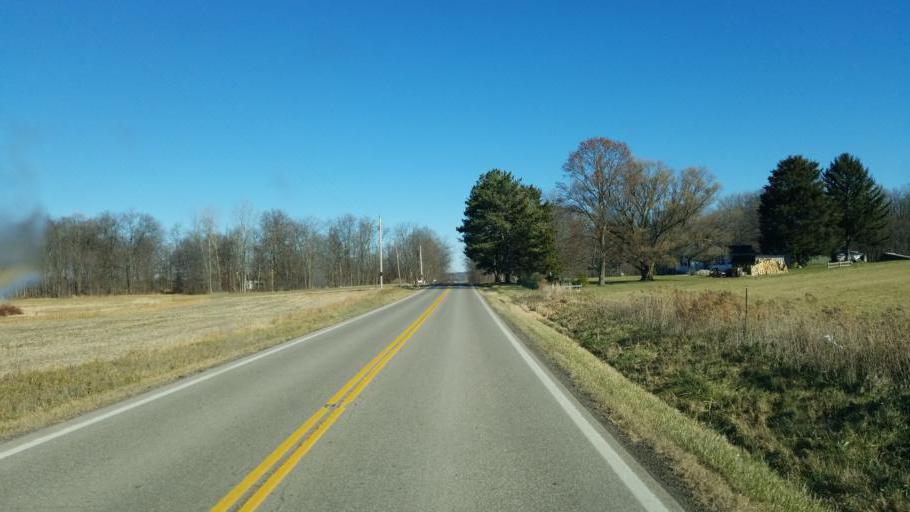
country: US
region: Ohio
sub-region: Ashland County
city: Ashland
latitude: 40.9432
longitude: -82.3843
